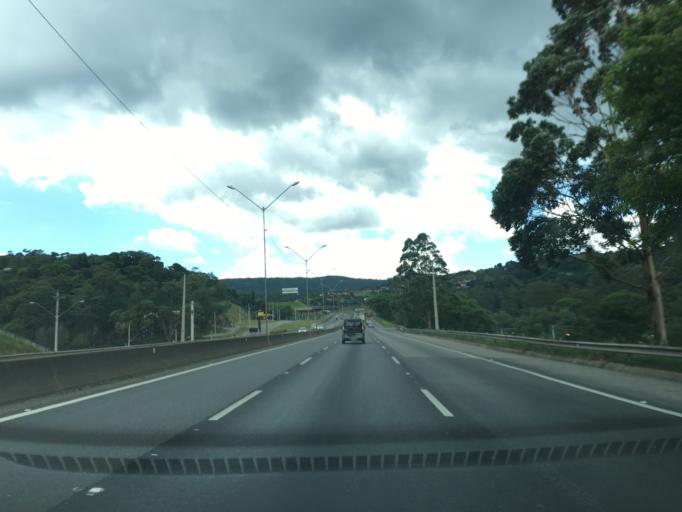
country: BR
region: Sao Paulo
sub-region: Mairipora
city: Mairipora
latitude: -23.3379
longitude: -46.5751
